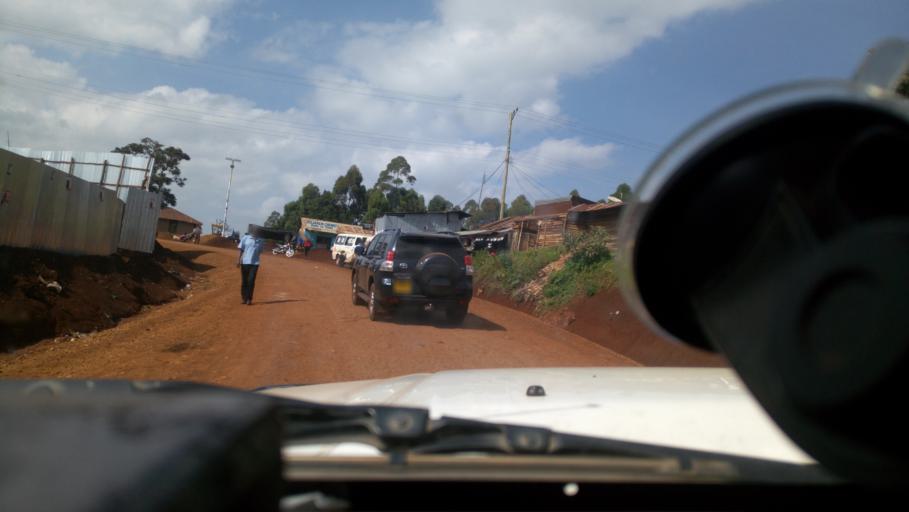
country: KE
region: Nyamira District
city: Nyamira
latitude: -0.6029
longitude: 34.9593
